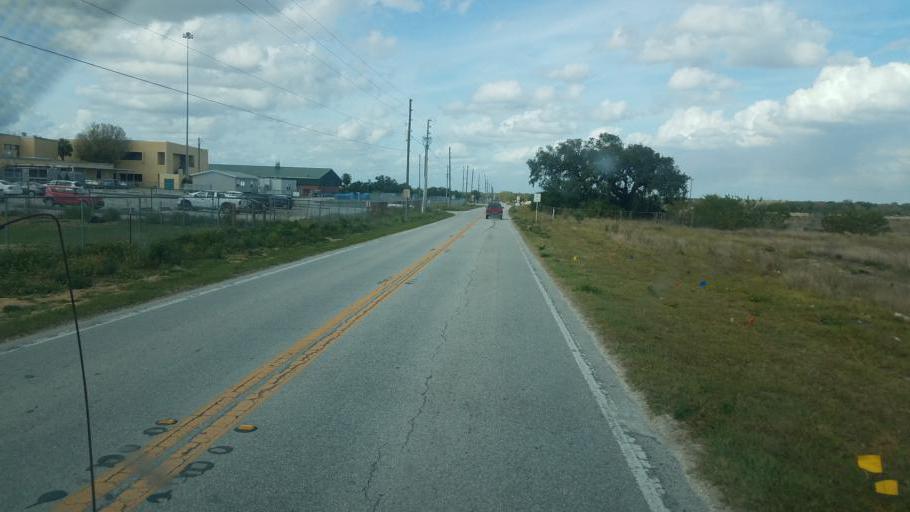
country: US
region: Florida
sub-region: Polk County
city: Haines City
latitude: 28.0975
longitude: -81.6068
